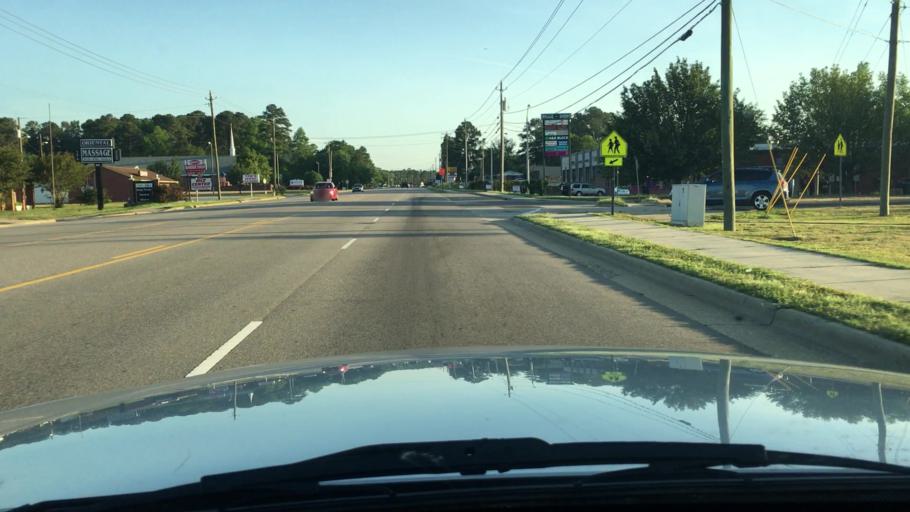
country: US
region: North Carolina
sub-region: Cumberland County
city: Fort Bragg
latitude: 35.0936
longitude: -79.0108
